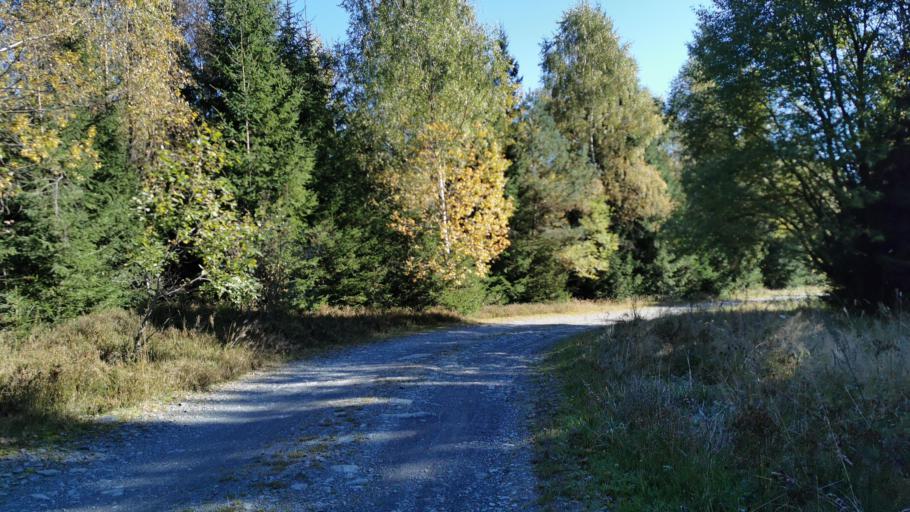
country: DE
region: Bavaria
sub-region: Upper Franconia
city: Tettau
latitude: 50.4861
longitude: 11.2894
